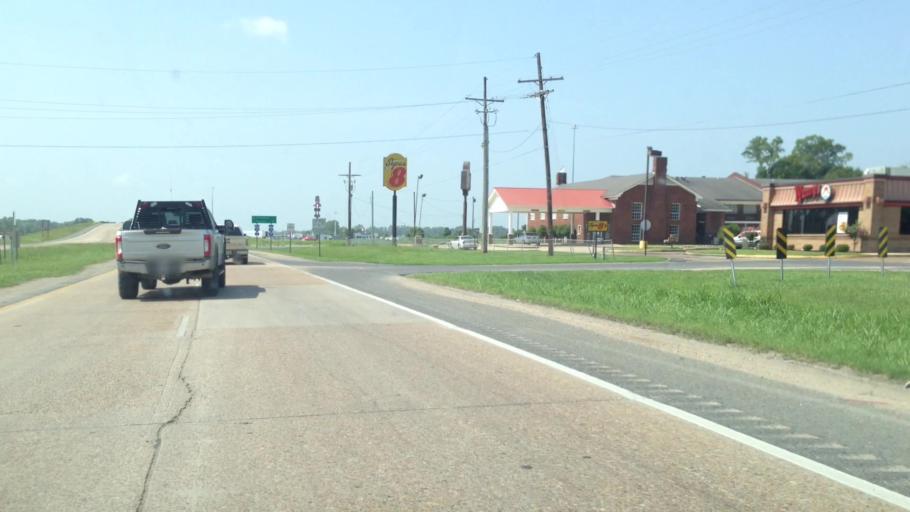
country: US
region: Louisiana
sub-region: Madison Parish
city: Tallulah
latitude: 32.3960
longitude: -91.1994
